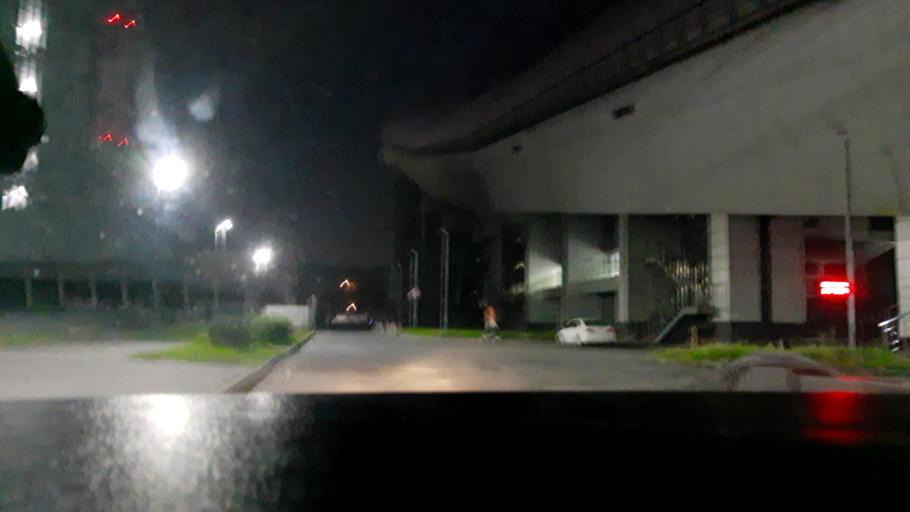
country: RU
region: Moskovskaya
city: Pavshino
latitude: 55.8151
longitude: 37.3630
